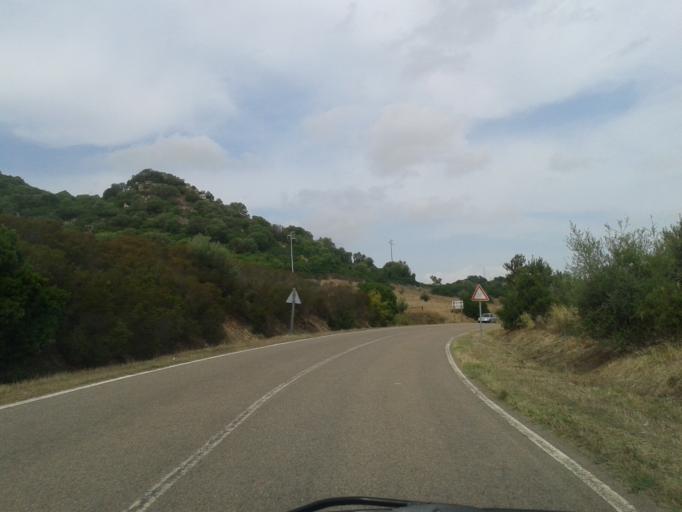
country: IT
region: Sardinia
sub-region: Provincia di Cagliari
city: Villasimius
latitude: 39.1876
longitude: 9.5590
